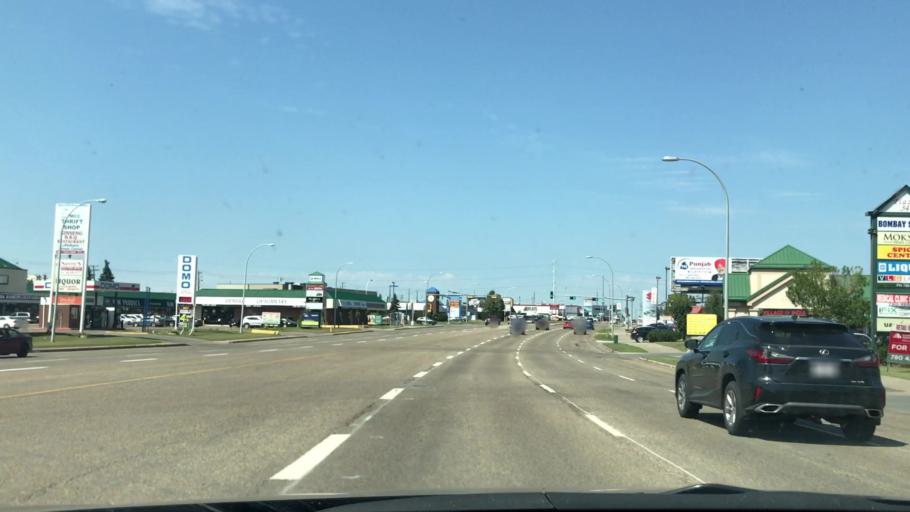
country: CA
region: Alberta
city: Edmonton
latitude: 53.4655
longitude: -113.4723
